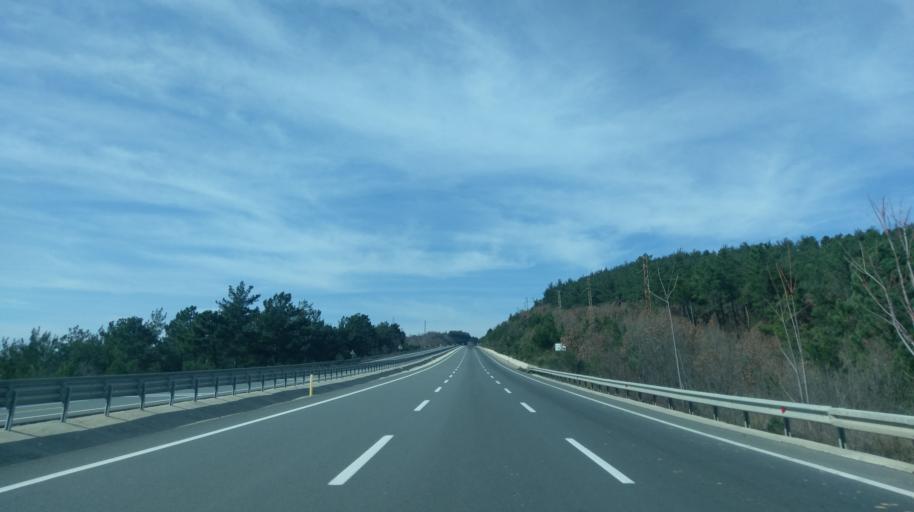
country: TR
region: Canakkale
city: Evrese
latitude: 40.7079
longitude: 26.7809
